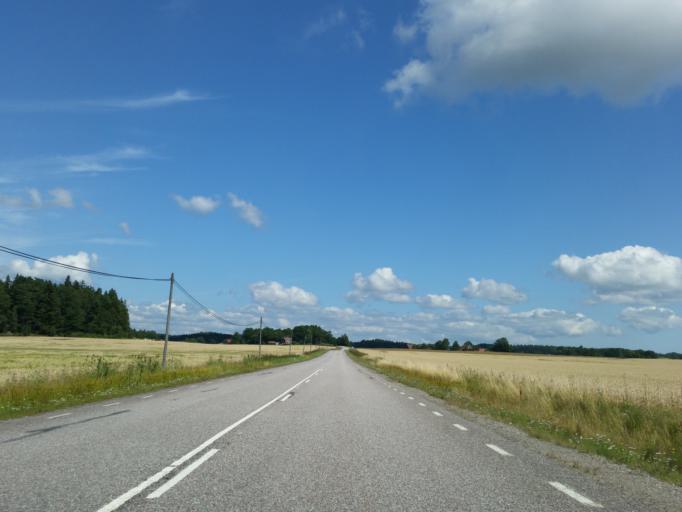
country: SE
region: Soedermanland
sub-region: Trosa Kommun
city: Vagnharad
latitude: 58.9876
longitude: 17.6365
